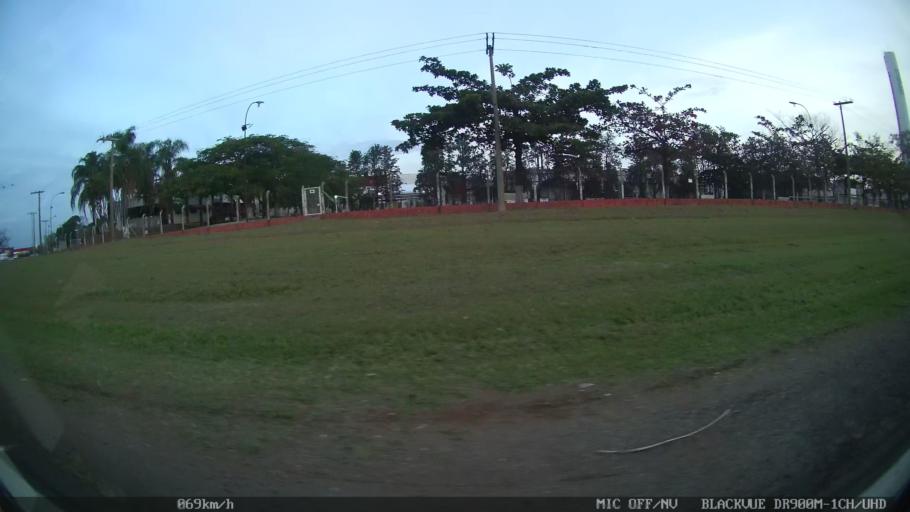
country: BR
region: Sao Paulo
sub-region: Limeira
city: Limeira
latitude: -22.5475
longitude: -47.3763
